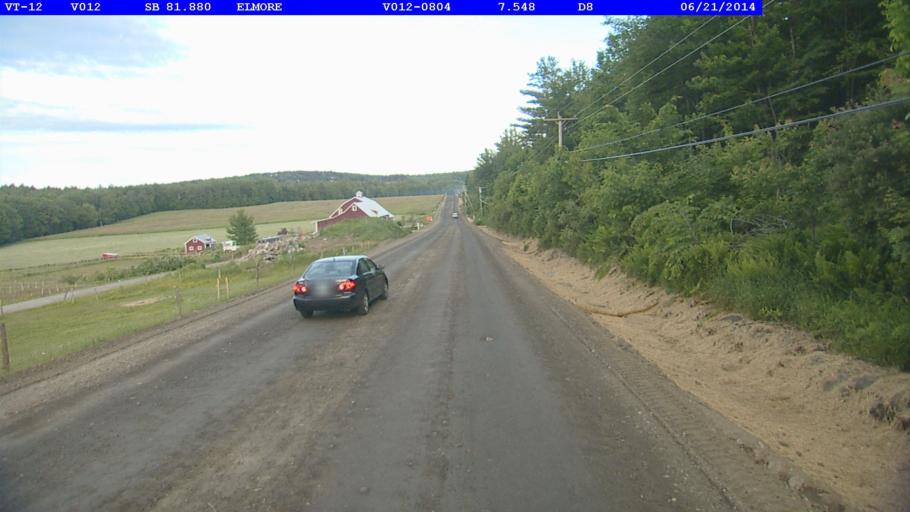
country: US
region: Vermont
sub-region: Lamoille County
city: Morrisville
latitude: 44.5491
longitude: -72.5344
